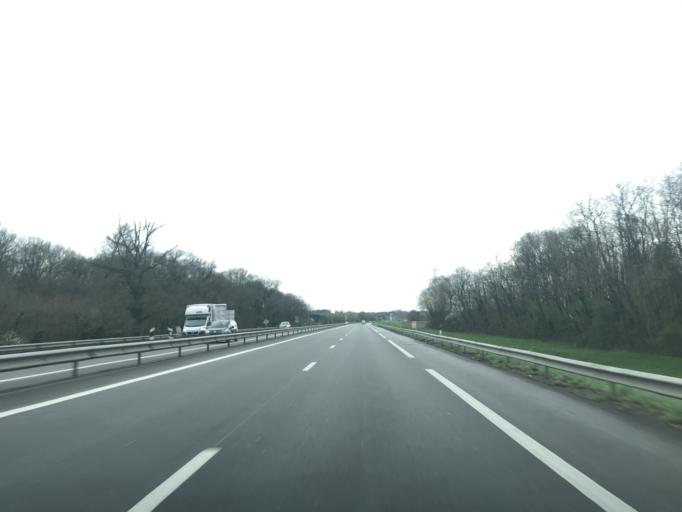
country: FR
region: Centre
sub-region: Departement du Loiret
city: Mardie
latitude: 47.9069
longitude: 2.0466
